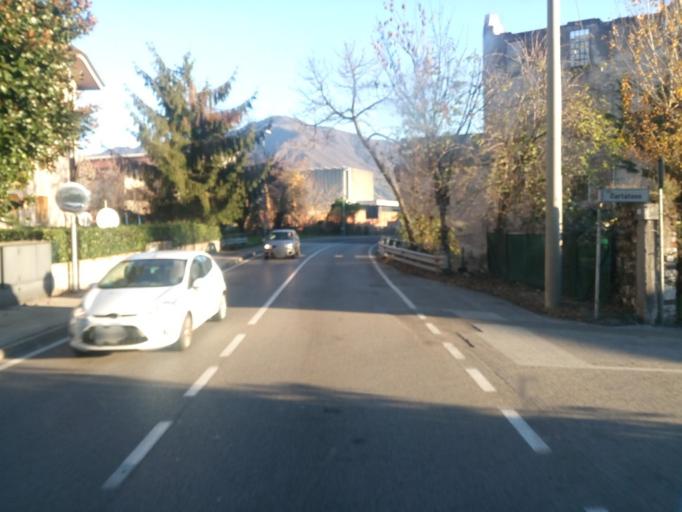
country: IT
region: Veneto
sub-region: Provincia di Vicenza
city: Schio
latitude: 45.7093
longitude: 11.3657
